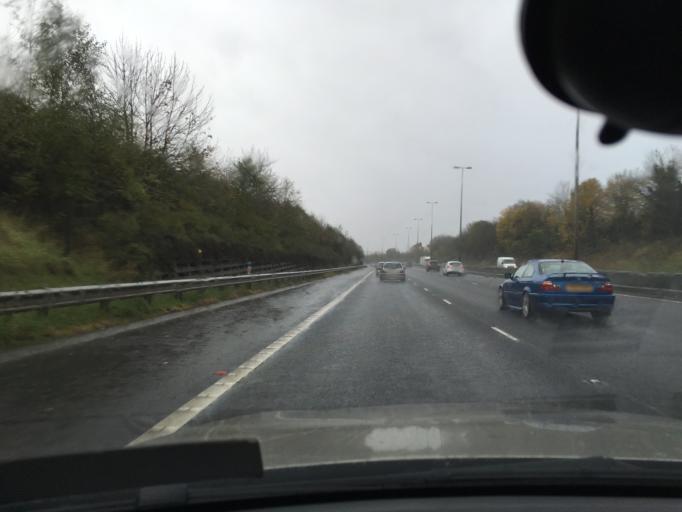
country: GB
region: Northern Ireland
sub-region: Newtownabbey District
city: Newtownabbey
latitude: 54.6536
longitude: -5.9290
